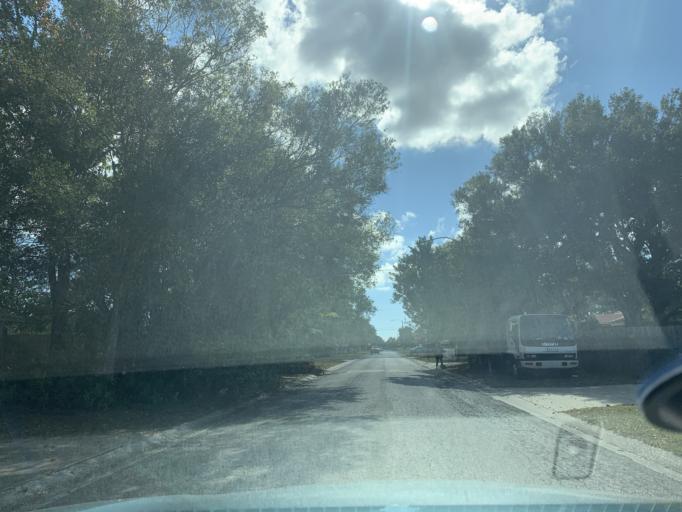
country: US
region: Florida
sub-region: Pinellas County
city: Kenneth City
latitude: 27.8062
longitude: -82.7383
